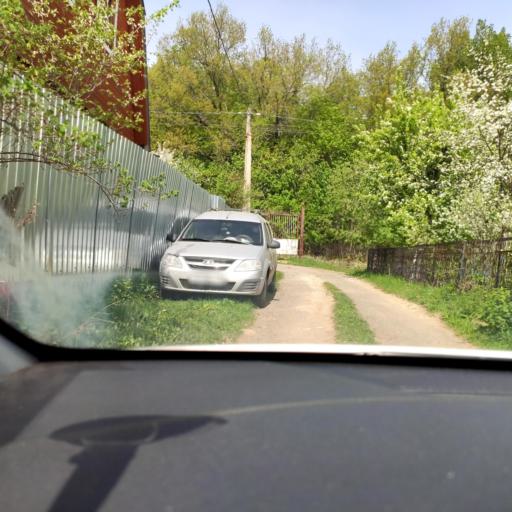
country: RU
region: Tatarstan
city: Osinovo
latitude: 55.7492
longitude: 48.8121
